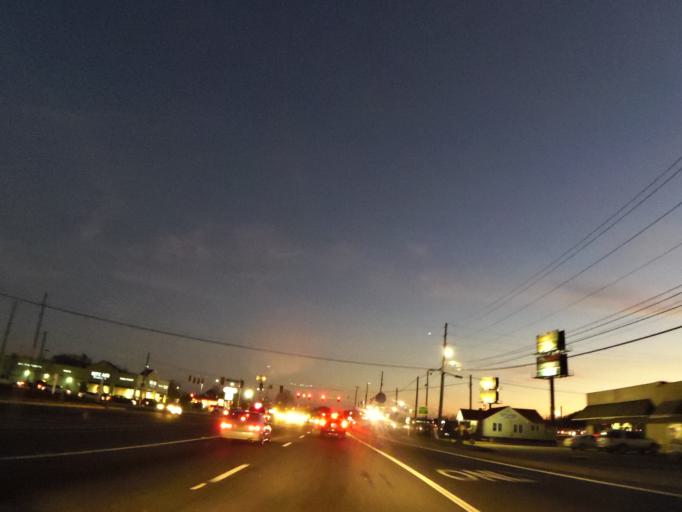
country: US
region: Georgia
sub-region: Whitfield County
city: Dalton
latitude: 34.7988
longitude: -84.9624
